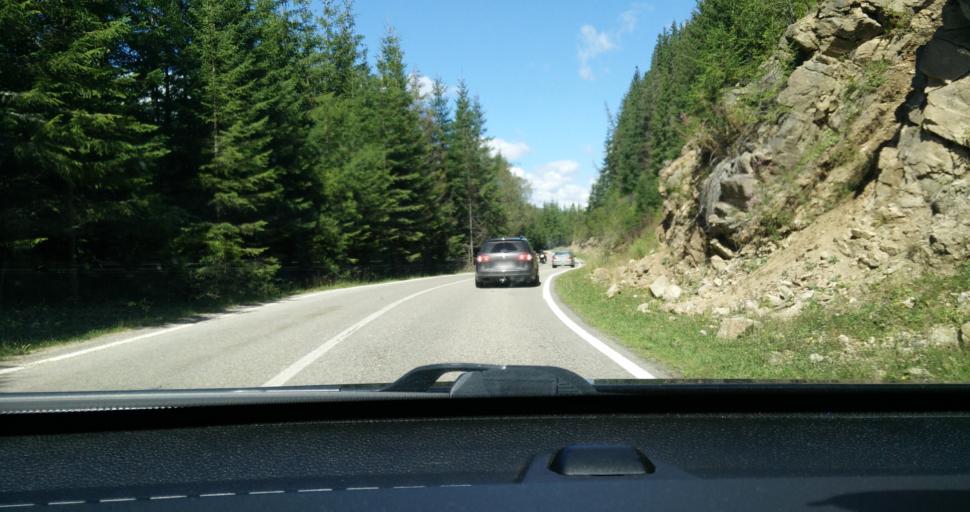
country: RO
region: Alba
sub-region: Comuna Sugag
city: Sugag
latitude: 45.5456
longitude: 23.6358
